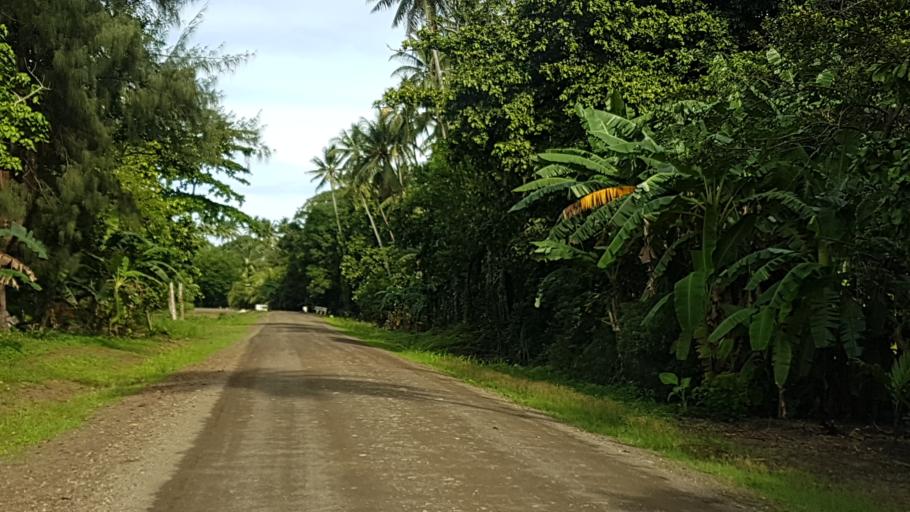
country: PG
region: Milne Bay
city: Alotau
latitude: -10.3236
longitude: 150.6844
